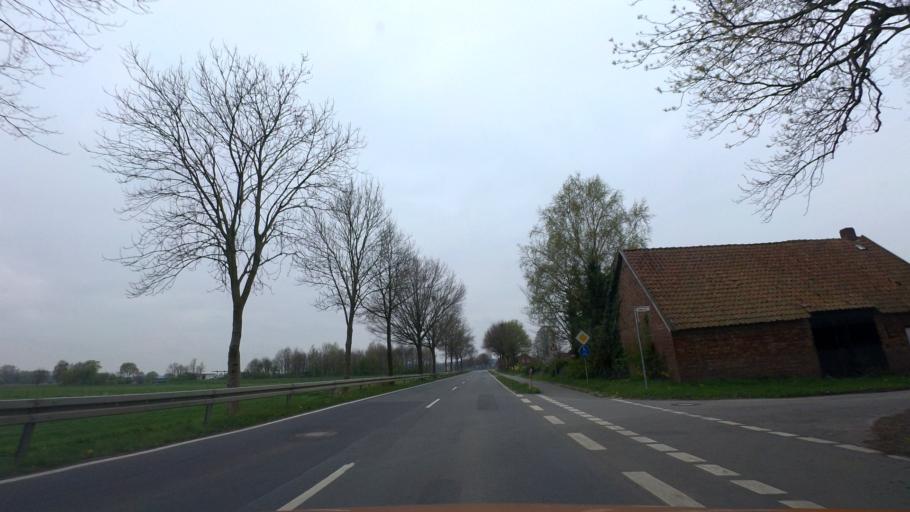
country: DE
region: Lower Saxony
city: Bramsche
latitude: 52.4388
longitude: 7.9960
